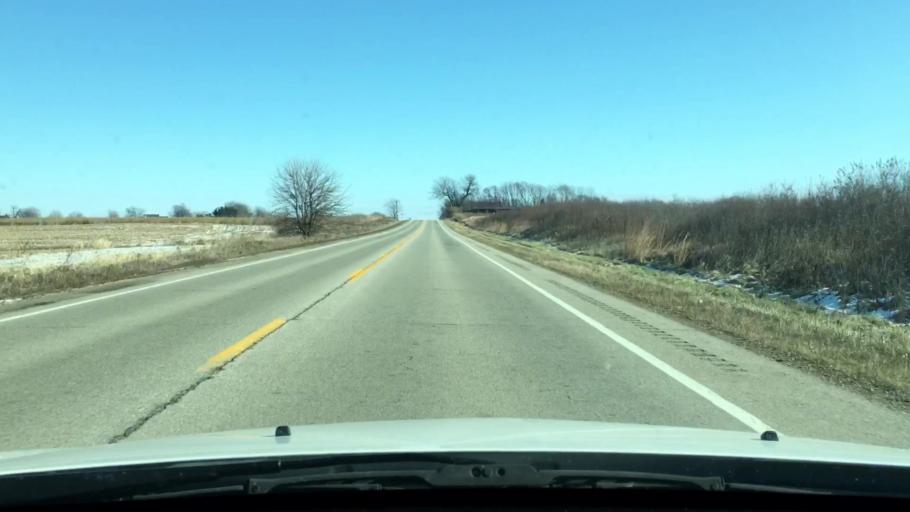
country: US
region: Illinois
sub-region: DeKalb County
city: Malta
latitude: 42.0009
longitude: -88.9053
